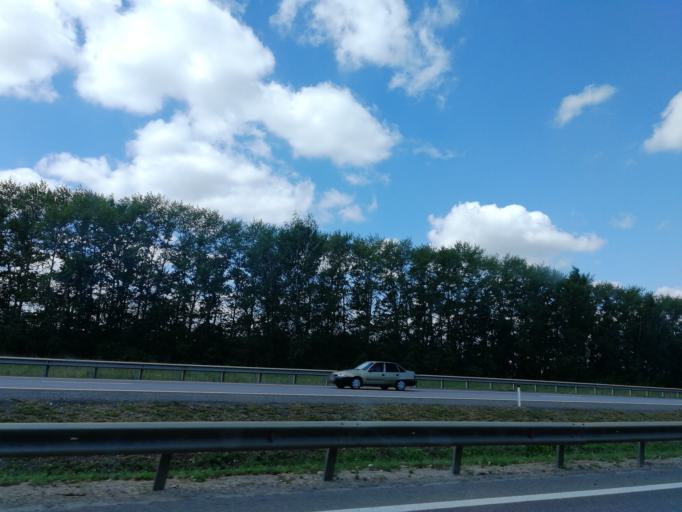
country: RU
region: Tula
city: Dubovka
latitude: 53.9208
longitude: 38.0413
